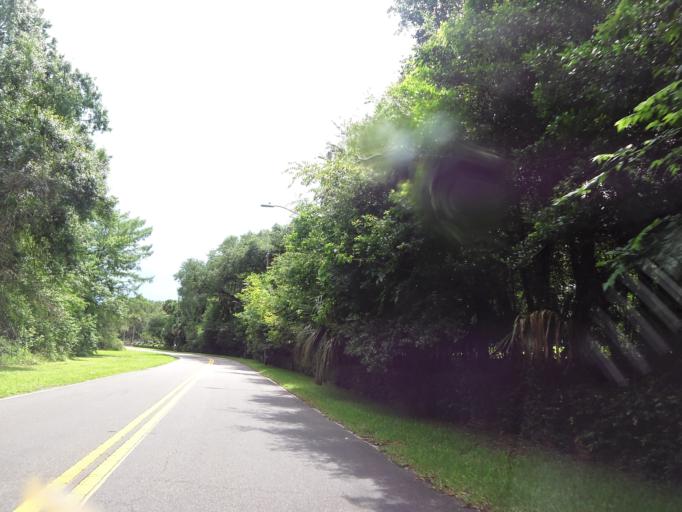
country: US
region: Florida
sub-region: Duval County
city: Jacksonville
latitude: 30.3667
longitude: -81.6420
